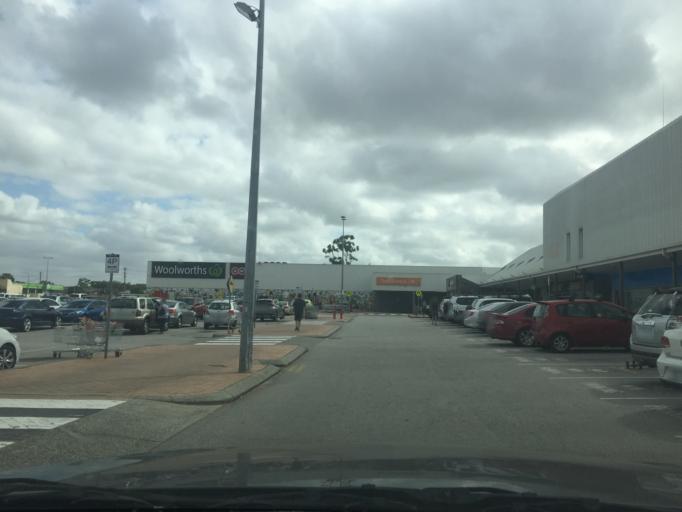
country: AU
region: Western Australia
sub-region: Gosnells
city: Maddington
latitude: -32.0530
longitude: 115.9795
